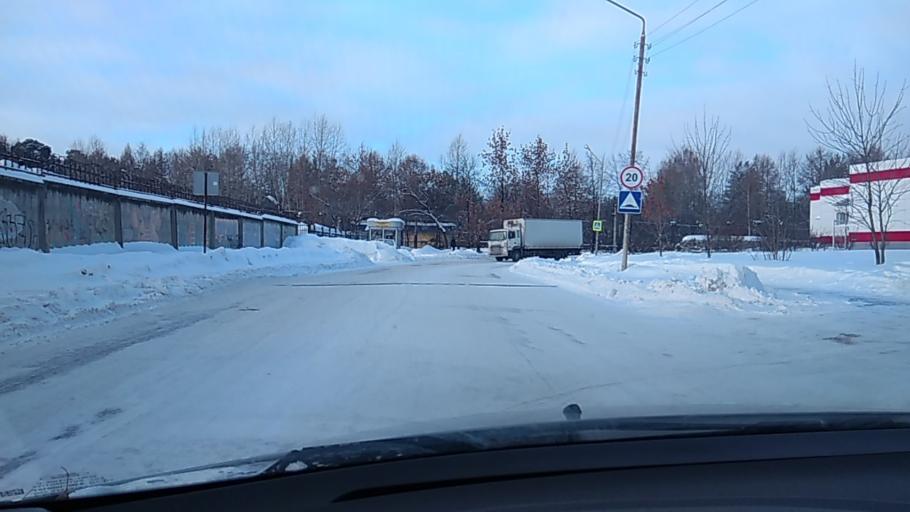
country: RU
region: Sverdlovsk
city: Yekaterinburg
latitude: 56.7927
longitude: 60.6083
